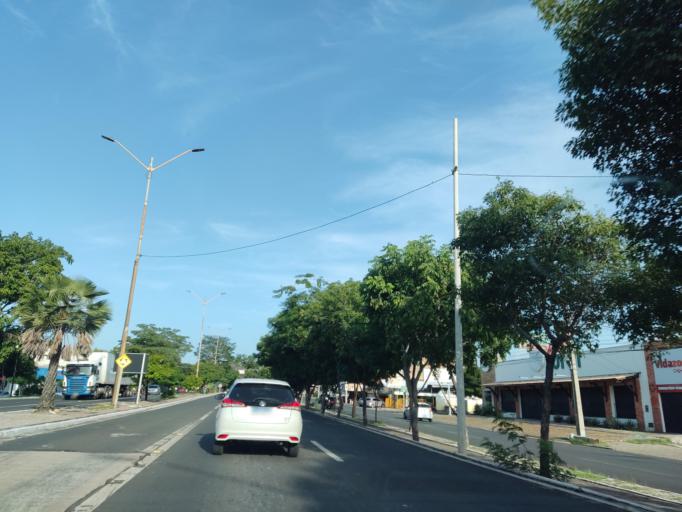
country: BR
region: Piaui
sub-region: Teresina
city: Teresina
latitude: -5.0812
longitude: -42.7776
